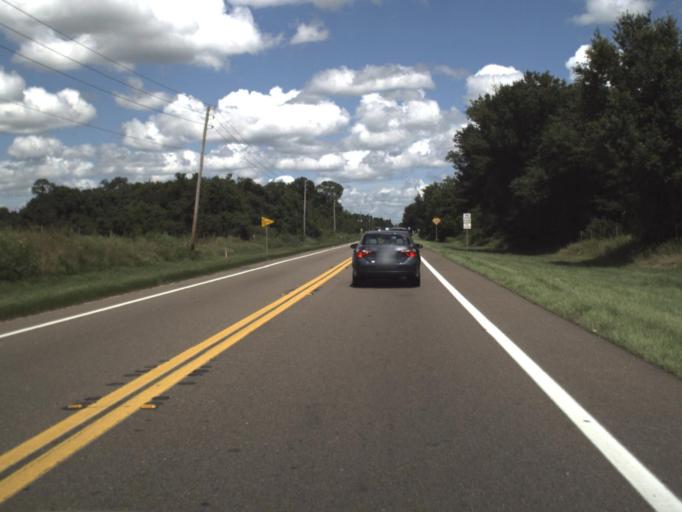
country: US
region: Florida
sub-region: Polk County
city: Lake Hamilton
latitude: 28.0728
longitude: -81.6721
